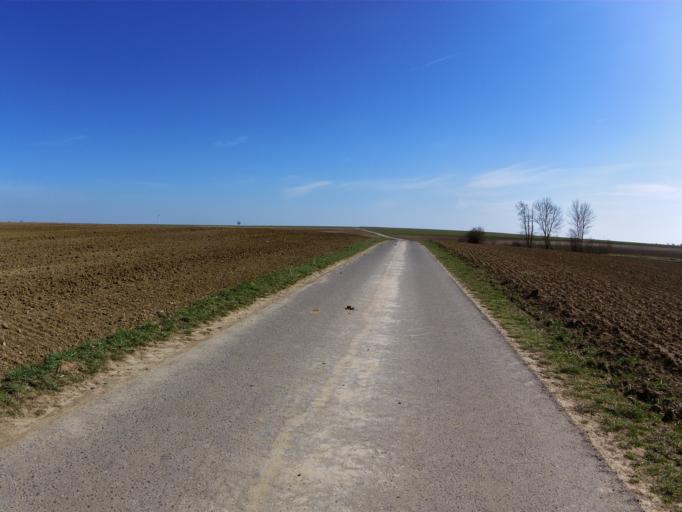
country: DE
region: Bavaria
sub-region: Regierungsbezirk Unterfranken
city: Prosselsheim
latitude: 49.8581
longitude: 10.1113
